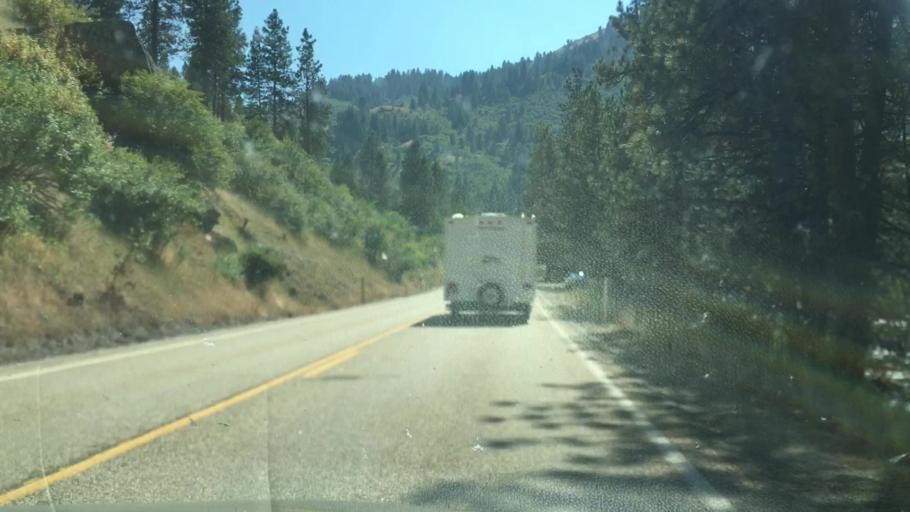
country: US
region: Idaho
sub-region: Boise County
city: Idaho City
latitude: 44.0560
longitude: -116.1282
